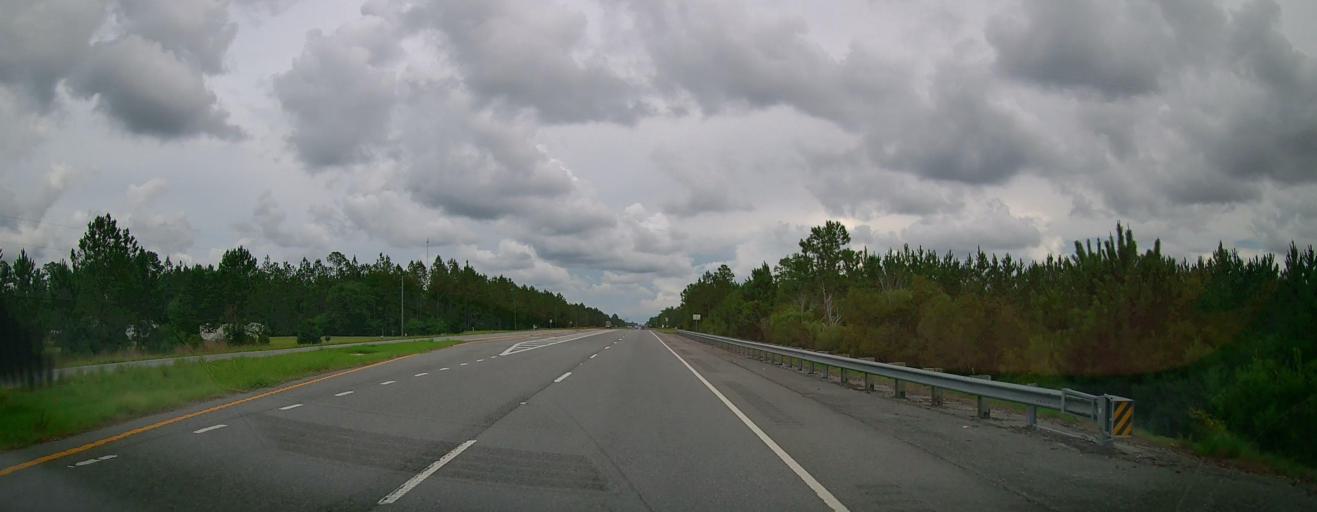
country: US
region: Georgia
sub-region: Wayne County
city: Jesup
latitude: 31.6867
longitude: -82.1120
